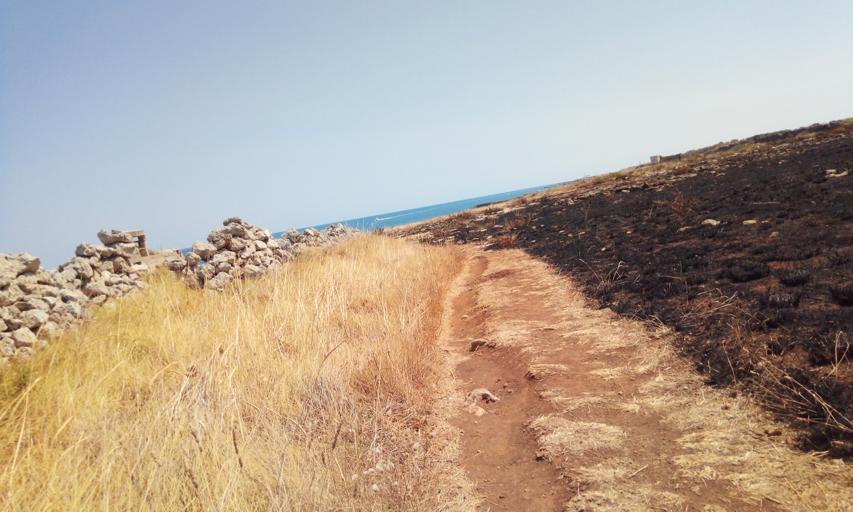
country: IT
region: Apulia
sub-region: Provincia di Bari
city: Polignano a Mare
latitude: 40.9844
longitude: 17.2491
